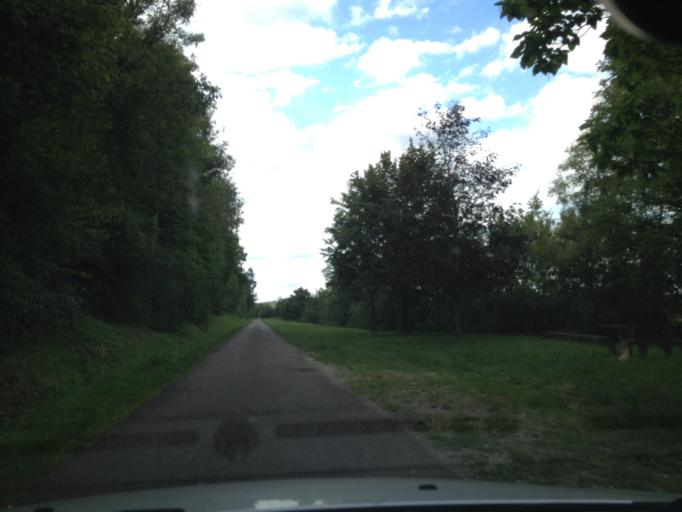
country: FR
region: Franche-Comte
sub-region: Departement de la Haute-Saone
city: Jussey
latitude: 47.7994
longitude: 5.9891
